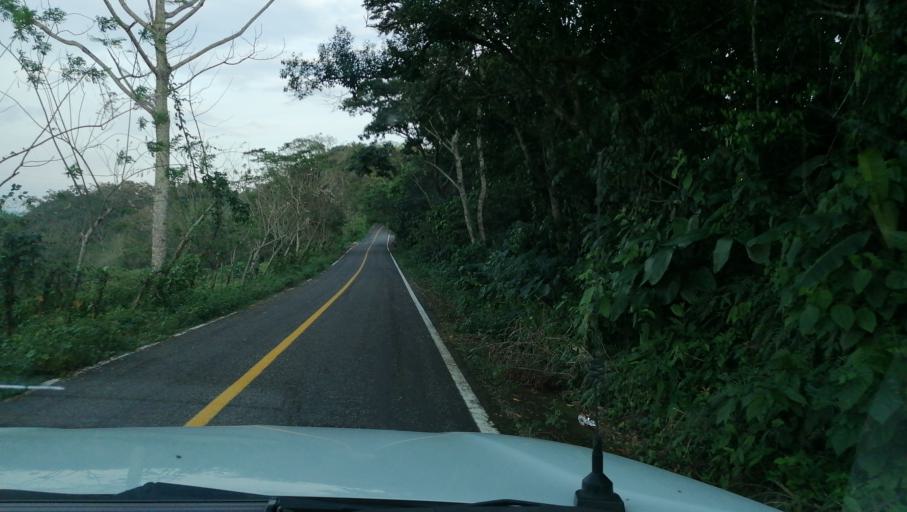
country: MX
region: Chiapas
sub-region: Juarez
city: El Triunfo 1ra. Seccion (Cardona)
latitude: 17.5055
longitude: -93.2226
